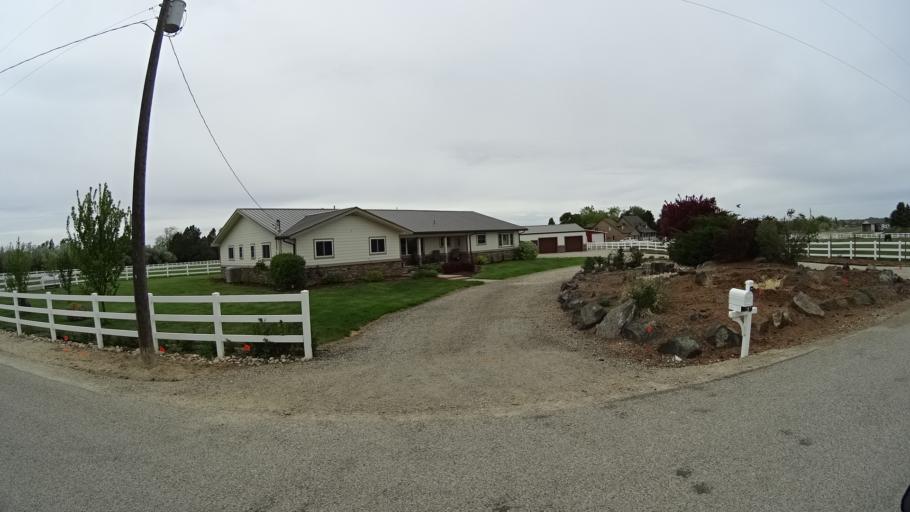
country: US
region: Idaho
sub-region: Ada County
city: Kuna
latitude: 43.4960
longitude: -116.3395
